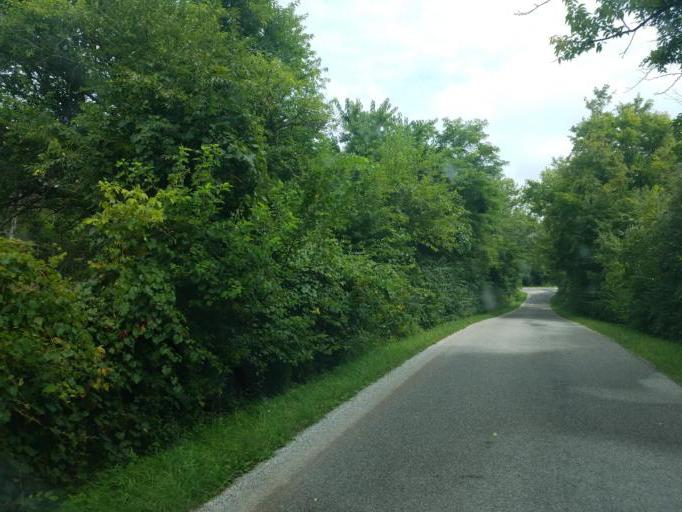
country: US
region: Ohio
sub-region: Morrow County
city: Cardington
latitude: 40.4162
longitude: -82.8506
